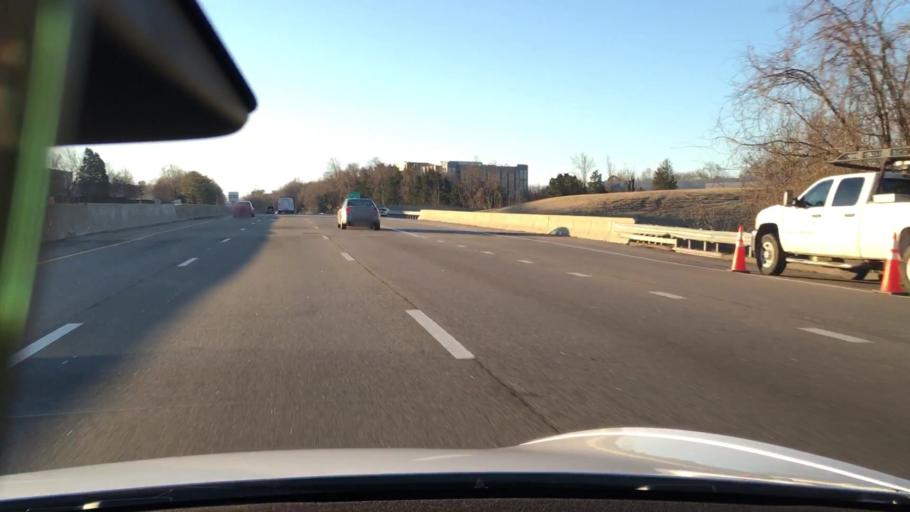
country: US
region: Virginia
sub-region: Chesterfield County
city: Bon Air
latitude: 37.5165
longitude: -77.5284
